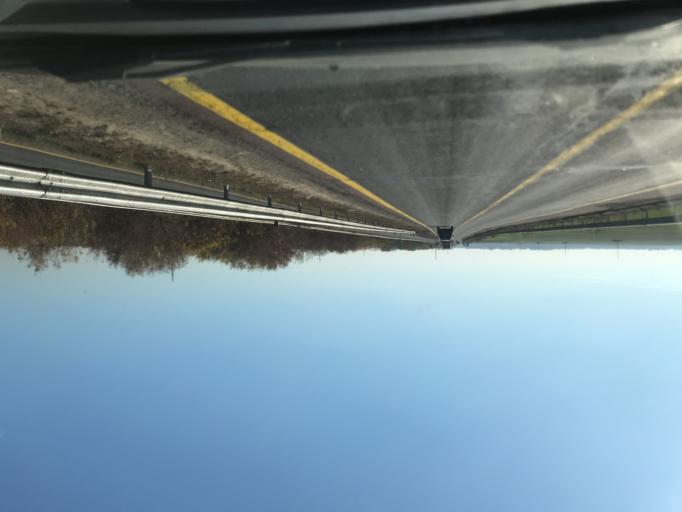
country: BY
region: Gomel
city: Horad Rechytsa
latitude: 52.3198
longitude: 30.5212
